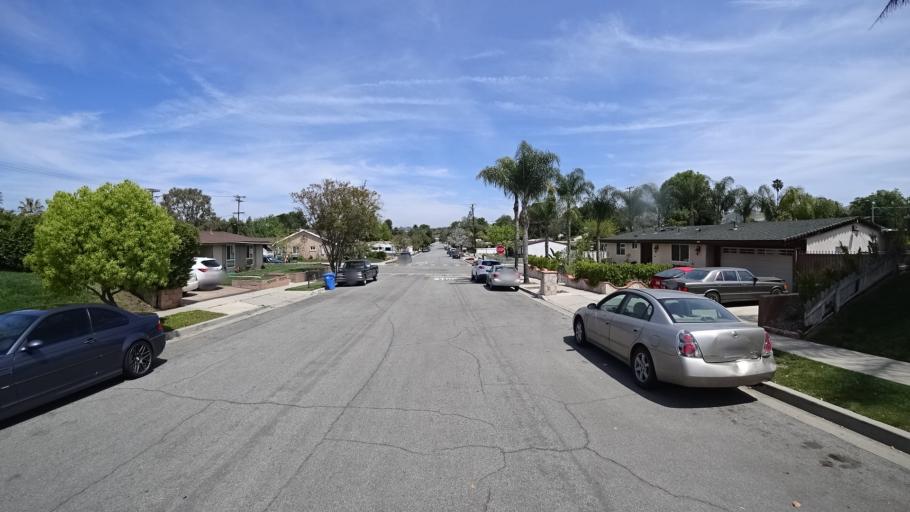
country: US
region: California
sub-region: Ventura County
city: Thousand Oaks
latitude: 34.1923
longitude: -118.8655
